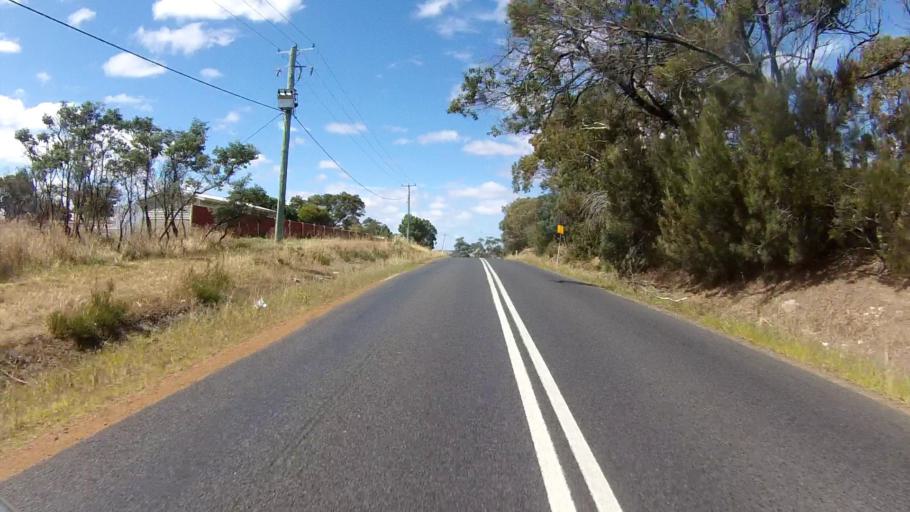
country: AU
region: Tasmania
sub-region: Sorell
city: Sorell
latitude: -42.6167
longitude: 147.4290
